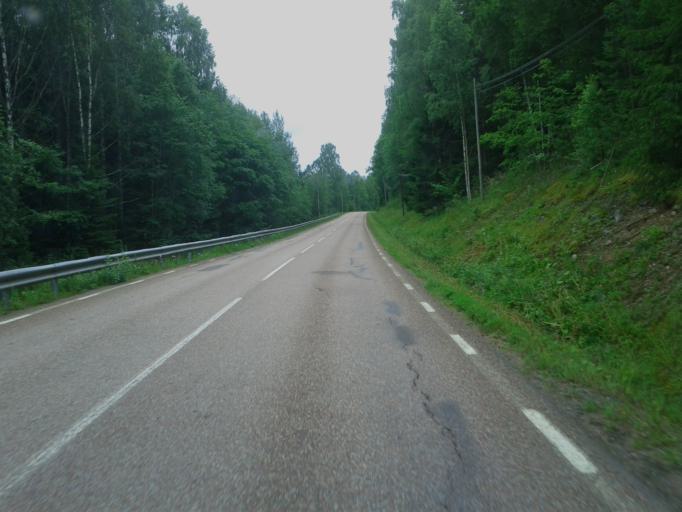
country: SE
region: Dalarna
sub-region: Smedjebackens Kommun
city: Smedjebacken
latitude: 60.3168
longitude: 15.3761
